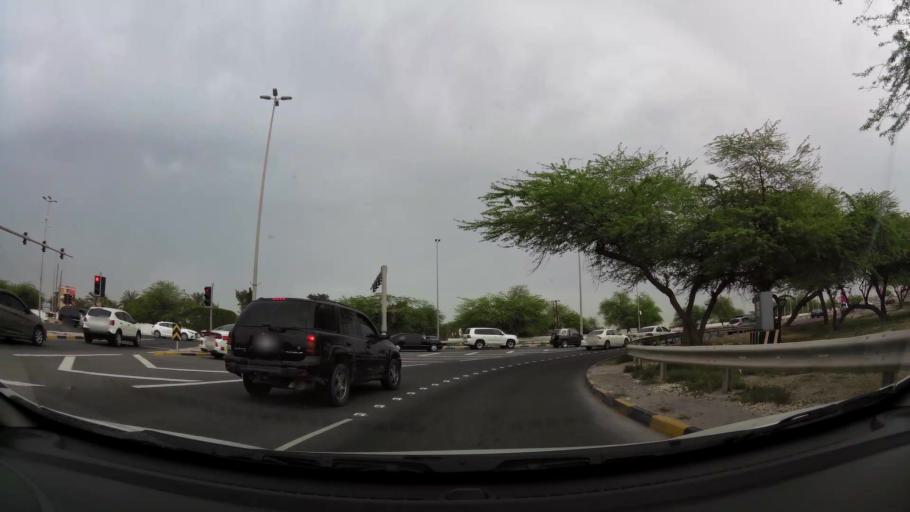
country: BH
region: Central Governorate
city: Dar Kulayb
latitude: 26.0566
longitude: 50.4999
